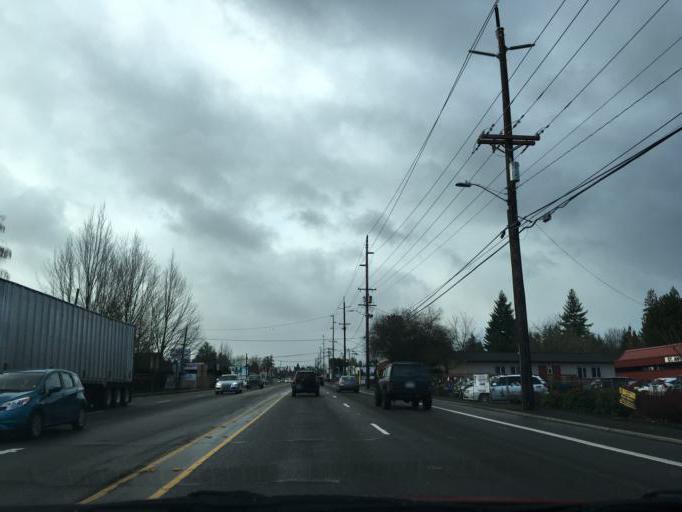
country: US
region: Oregon
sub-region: Washington County
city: Tigard
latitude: 45.4286
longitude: -122.7759
